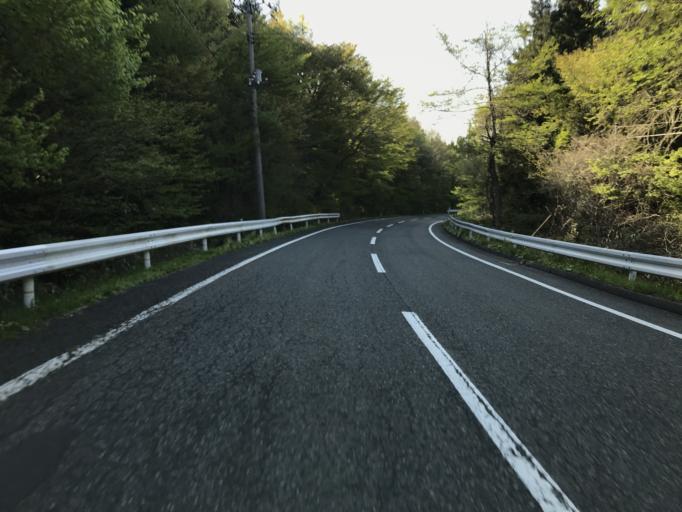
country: JP
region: Fukushima
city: Funehikimachi-funehiki
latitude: 37.5375
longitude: 140.7424
